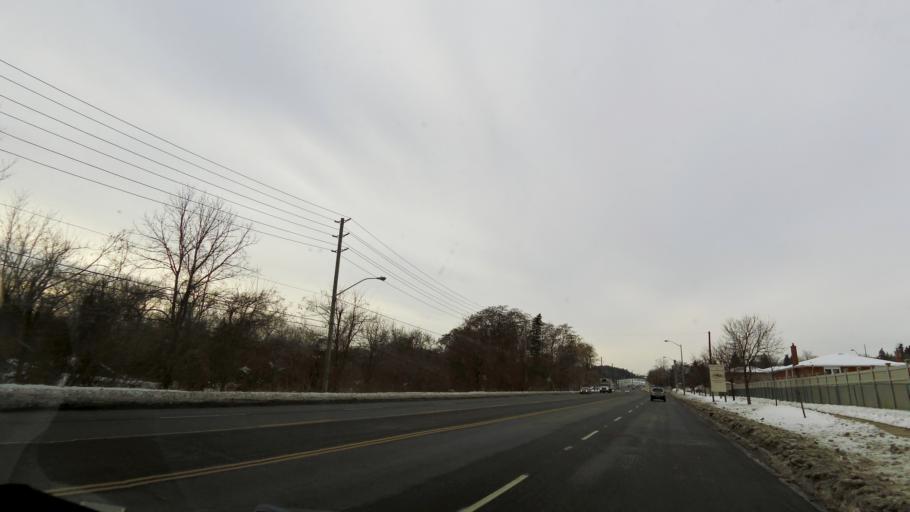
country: CA
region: Ontario
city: Concord
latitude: 43.7779
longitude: -79.5841
